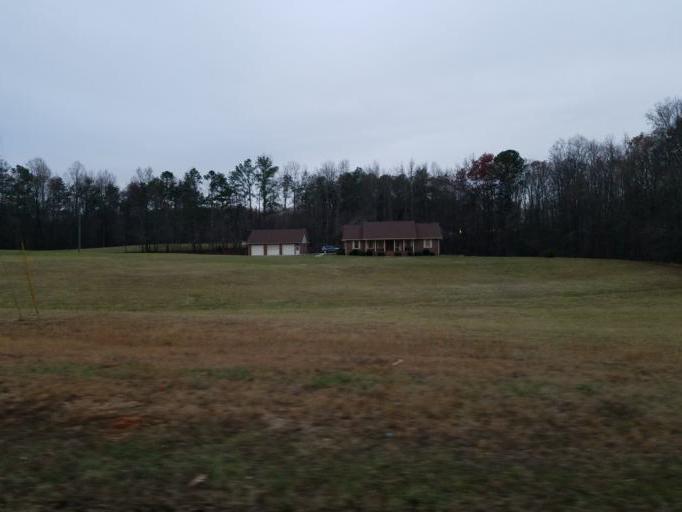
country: US
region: Georgia
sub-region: Dawson County
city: Dawsonville
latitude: 34.4608
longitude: -84.1432
